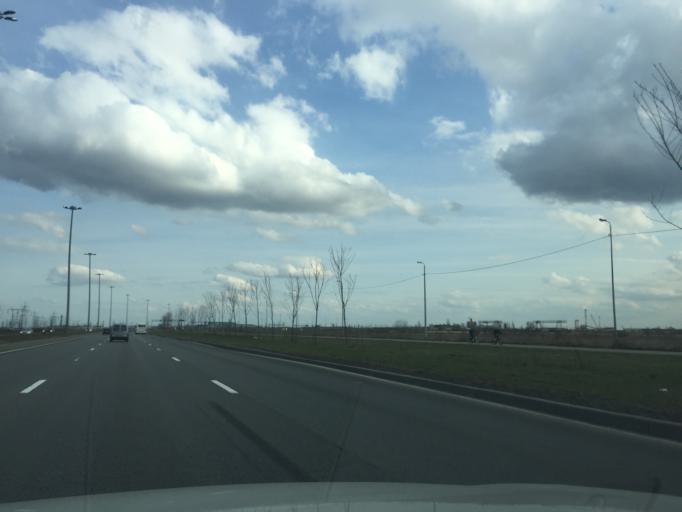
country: RU
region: St.-Petersburg
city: Petro-Slavyanka
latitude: 59.7987
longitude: 30.4871
